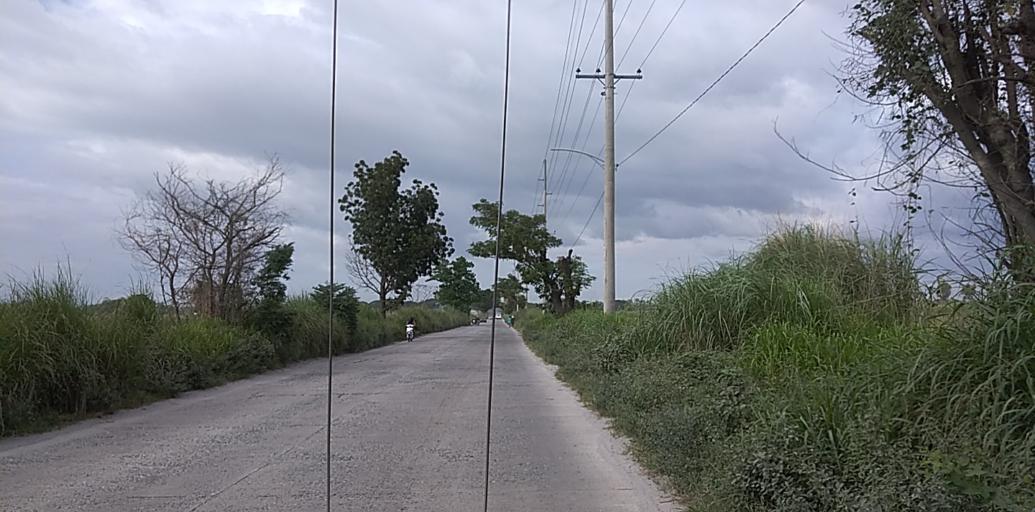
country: PH
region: Central Luzon
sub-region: Province of Pampanga
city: Porac
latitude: 15.0710
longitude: 120.5500
